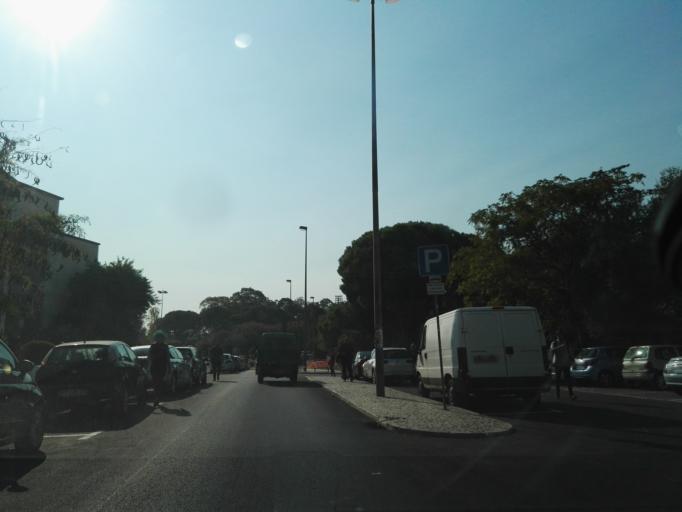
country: PT
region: Lisbon
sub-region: Odivelas
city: Olival do Basto
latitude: 38.7533
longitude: -9.1581
